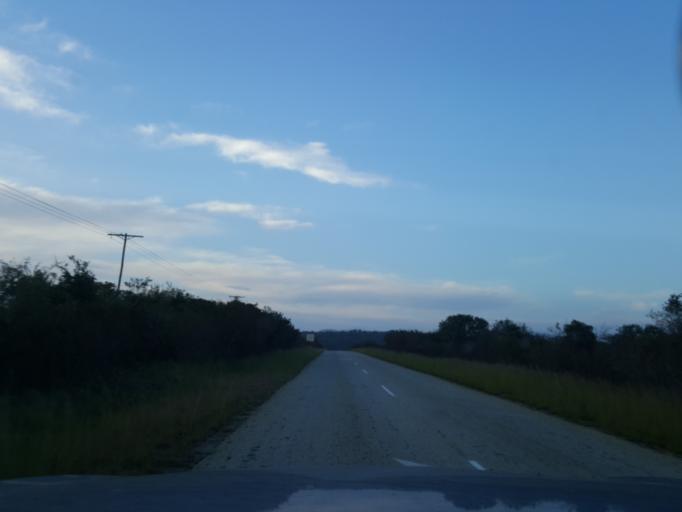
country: ZA
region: Eastern Cape
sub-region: Cacadu District Municipality
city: Grahamstown
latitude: -33.4148
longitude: 26.4745
